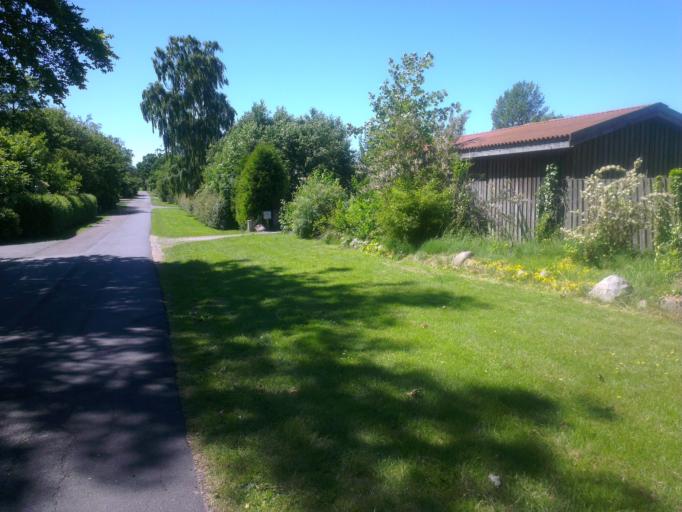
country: DK
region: Capital Region
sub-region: Halsnaes Kommune
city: Hundested
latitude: 55.9169
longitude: 11.9136
